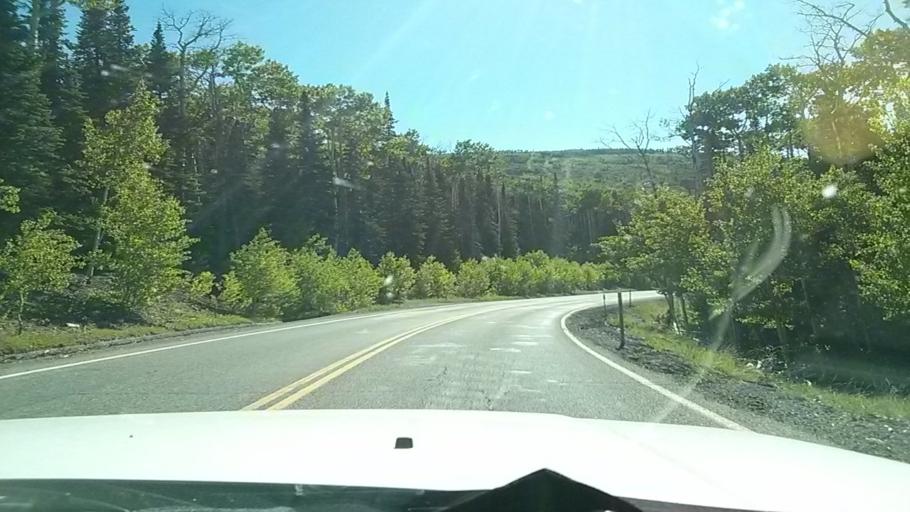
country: US
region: Utah
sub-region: Wayne County
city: Loa
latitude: 38.0698
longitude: -111.3315
